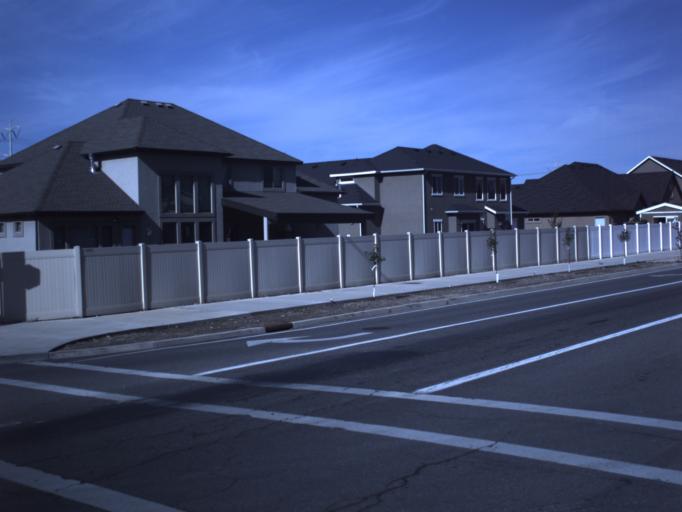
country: US
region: Utah
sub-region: Utah County
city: Orem
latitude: 40.2524
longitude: -111.7060
